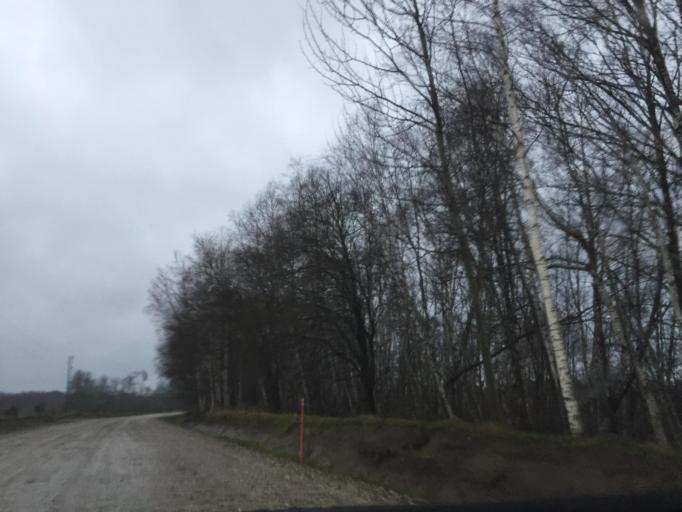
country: LV
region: Salacgrivas
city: Salacgriva
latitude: 57.7558
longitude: 24.4522
